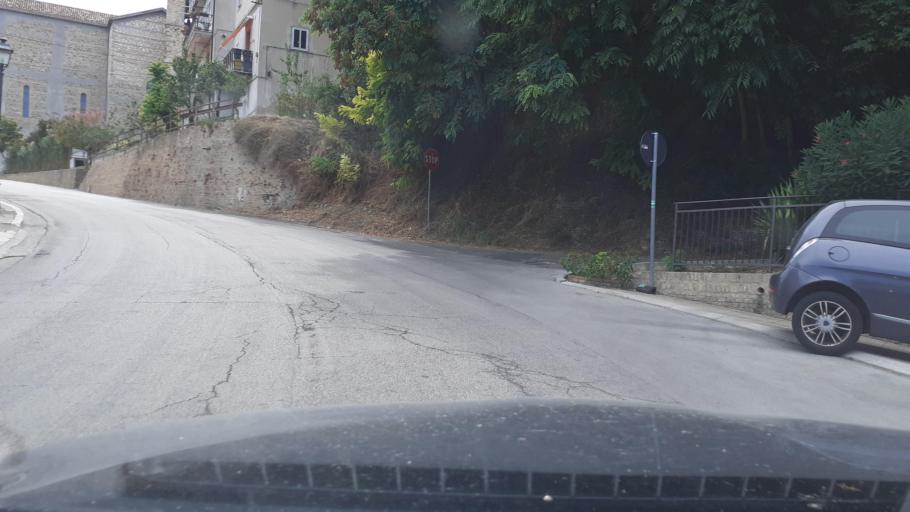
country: IT
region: Abruzzo
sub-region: Provincia di Chieti
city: Fossacesia
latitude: 42.2463
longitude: 14.4790
